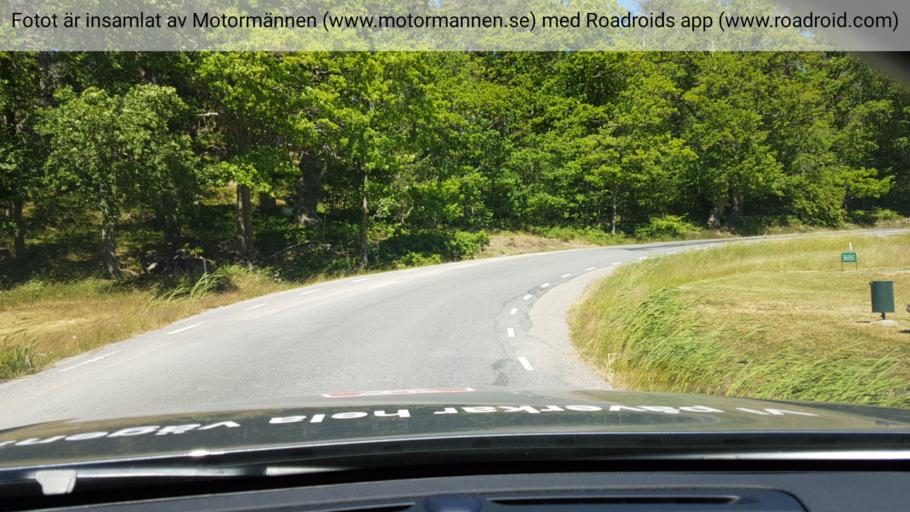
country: SE
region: Stockholm
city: Dalaro
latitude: 59.1636
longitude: 18.4485
